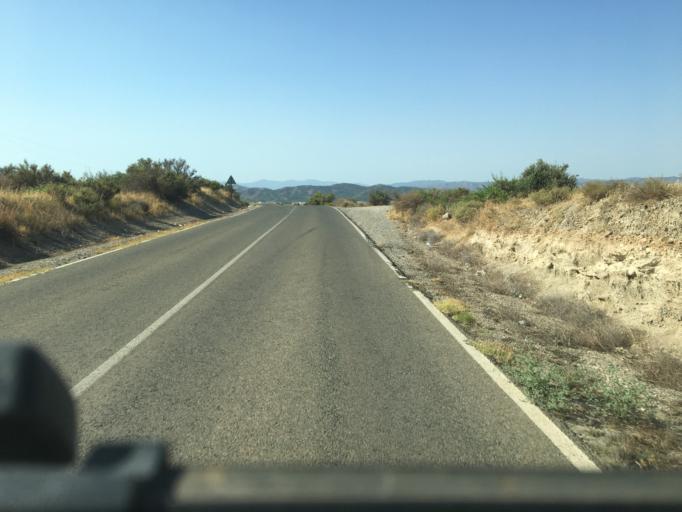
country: ES
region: Andalusia
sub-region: Provincia de Almeria
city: Huercal-Overa
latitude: 37.4273
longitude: -1.9713
